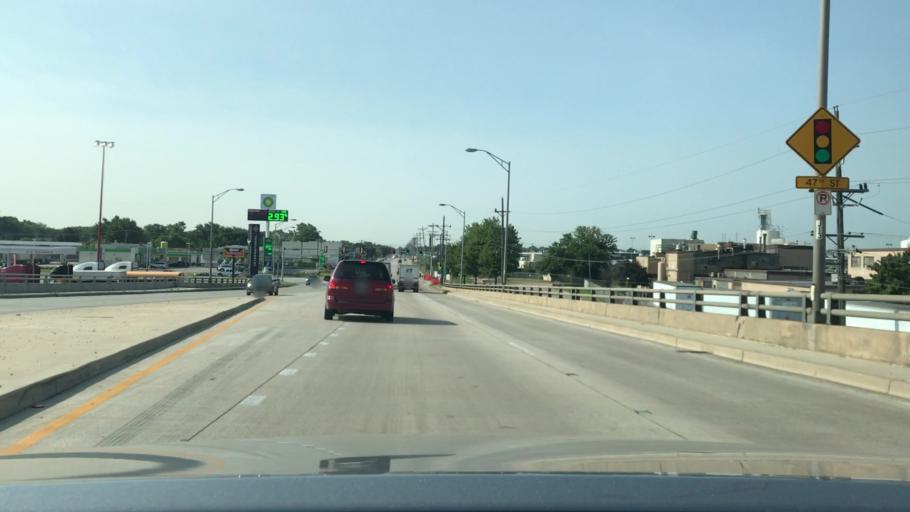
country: US
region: Illinois
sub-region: Cook County
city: Stickney
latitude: 41.8091
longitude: -87.7629
